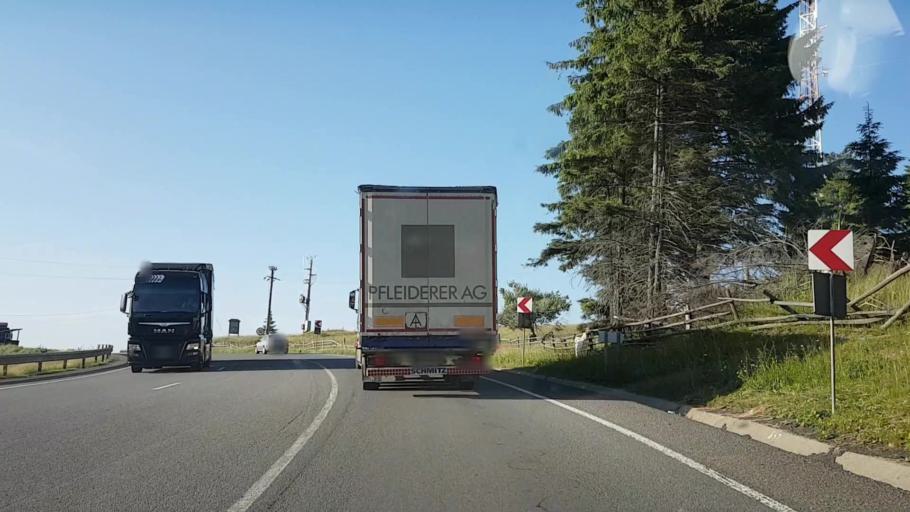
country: RO
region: Bistrita-Nasaud
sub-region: Comuna Lunca Ilvei
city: Lunca Ilvei
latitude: 47.2654
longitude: 25.0203
